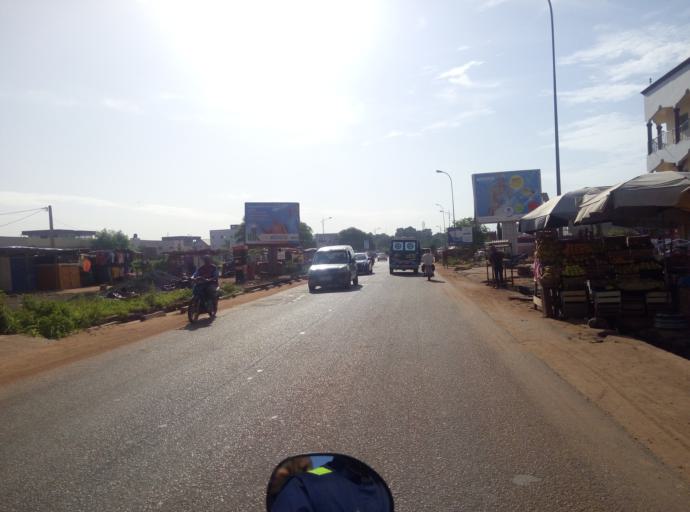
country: ML
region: Bamako
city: Bamako
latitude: 12.6536
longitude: -7.9332
